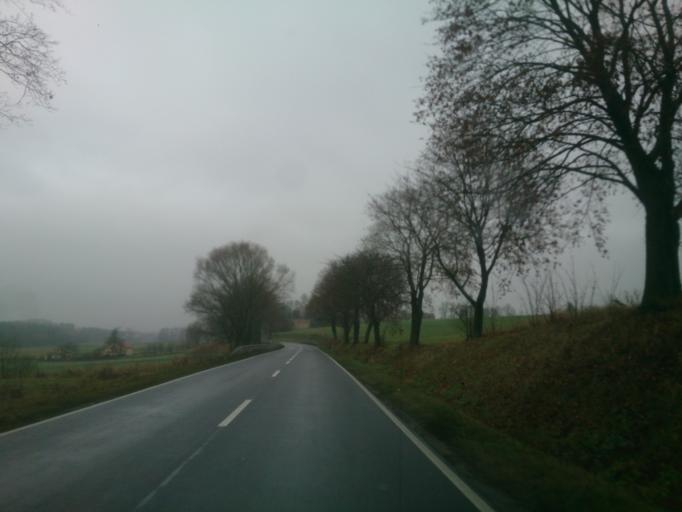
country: PL
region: Kujawsko-Pomorskie
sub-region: Powiat rypinski
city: Rypin
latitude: 53.1315
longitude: 19.3849
